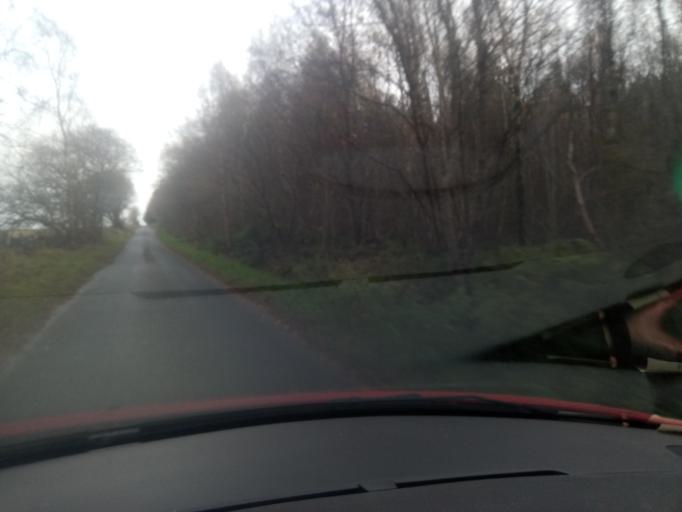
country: GB
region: Scotland
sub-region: The Scottish Borders
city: Jedburgh
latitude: 55.4847
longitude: -2.5889
